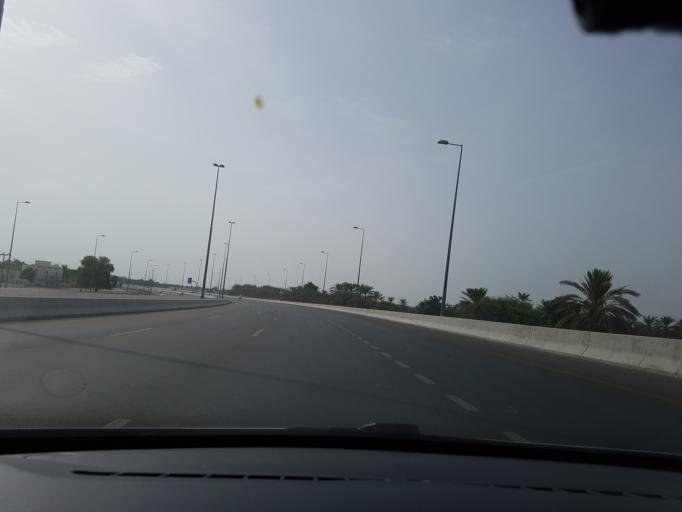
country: OM
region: Al Batinah
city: Al Sohar
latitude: 24.3464
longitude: 56.7174
